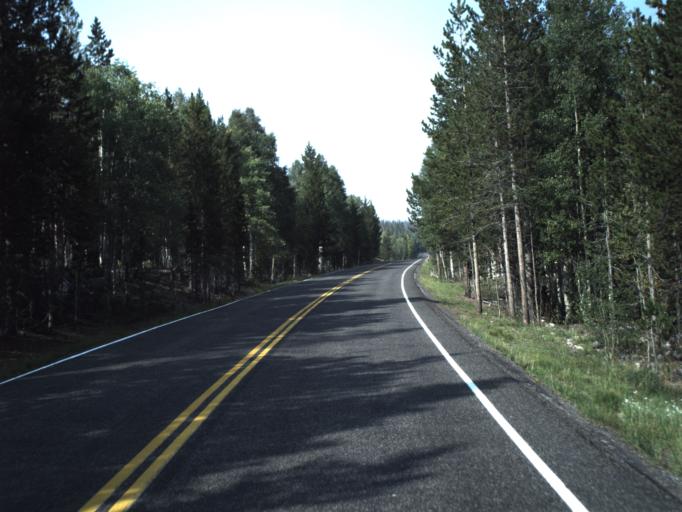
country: US
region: Utah
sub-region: Summit County
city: Oakley
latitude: 40.7989
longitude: -110.8826
